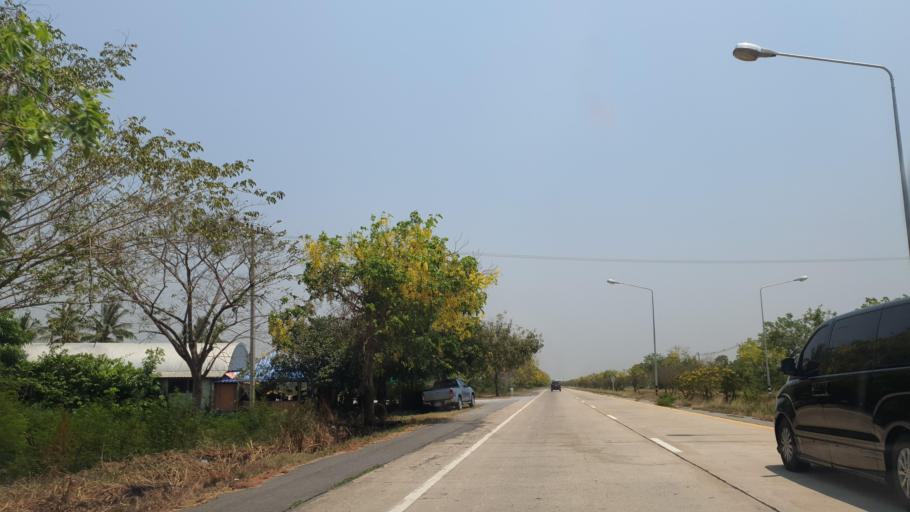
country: TH
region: Suphan Buri
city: Suphan Buri
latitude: 14.5072
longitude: 100.0503
